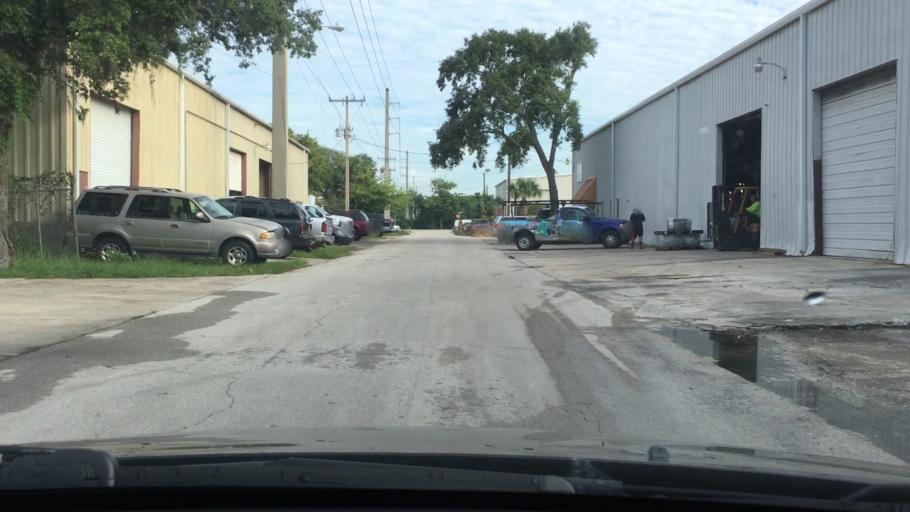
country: US
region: Florida
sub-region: Volusia County
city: Holly Hill
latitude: 29.2529
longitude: -81.0493
